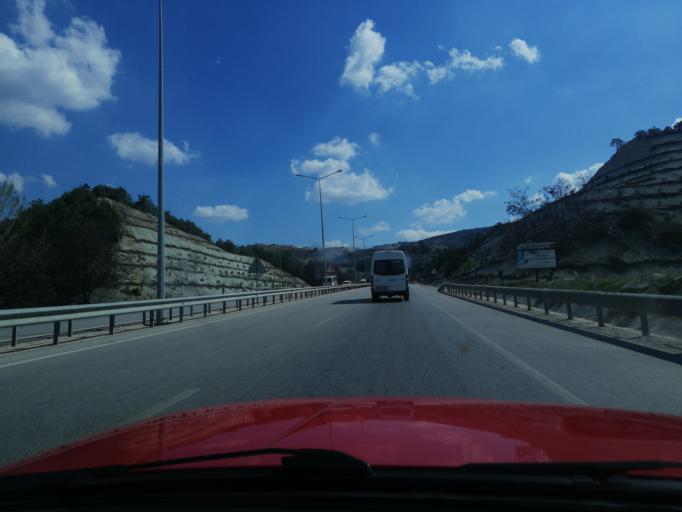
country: TR
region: Burdur
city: Burdur
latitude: 37.7054
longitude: 30.3062
